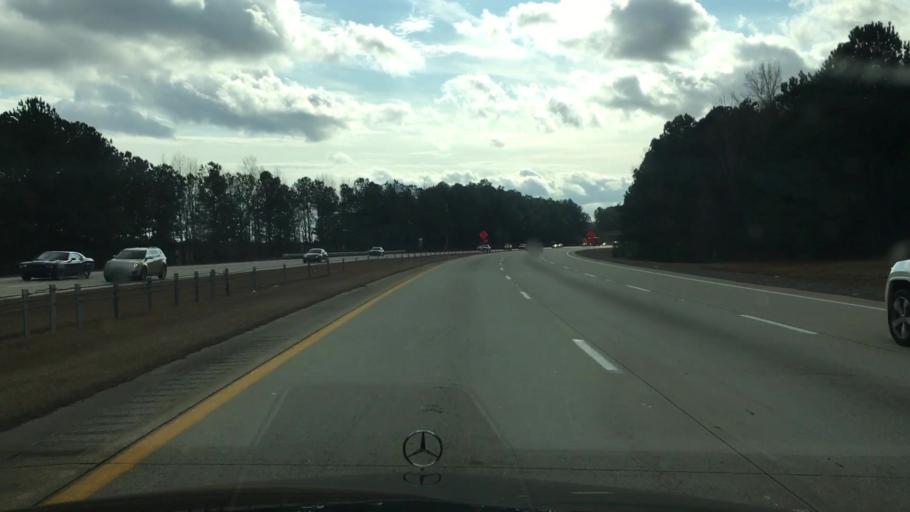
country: US
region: North Carolina
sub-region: Johnston County
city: Clayton
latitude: 35.6022
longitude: -78.5635
